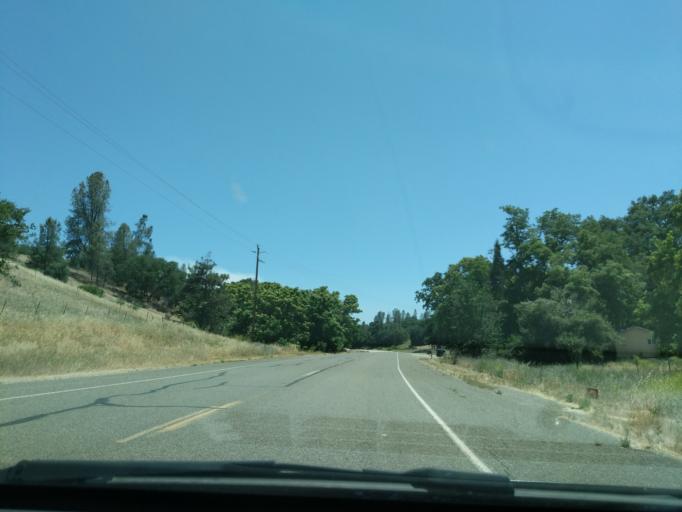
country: US
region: California
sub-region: Monterey County
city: King City
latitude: 36.0501
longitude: -121.1819
